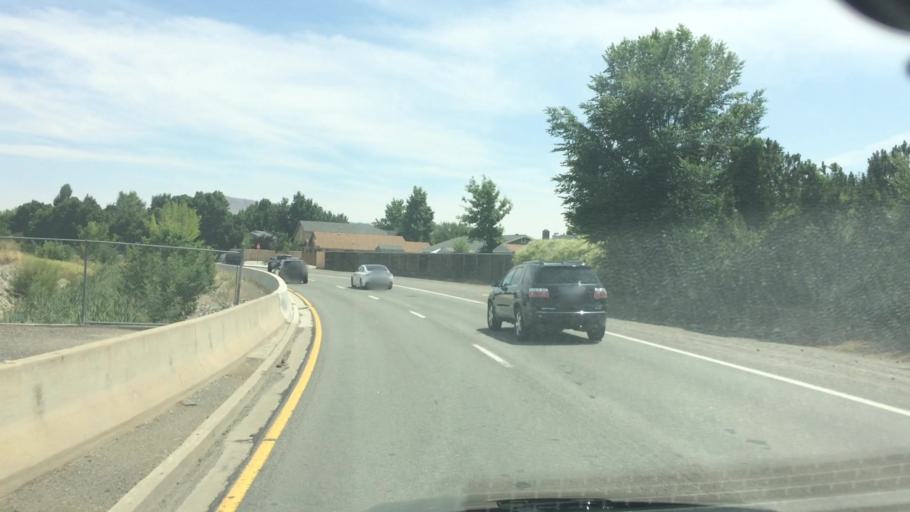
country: US
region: Nevada
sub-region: Washoe County
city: Sparks
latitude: 39.5554
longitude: -119.7244
